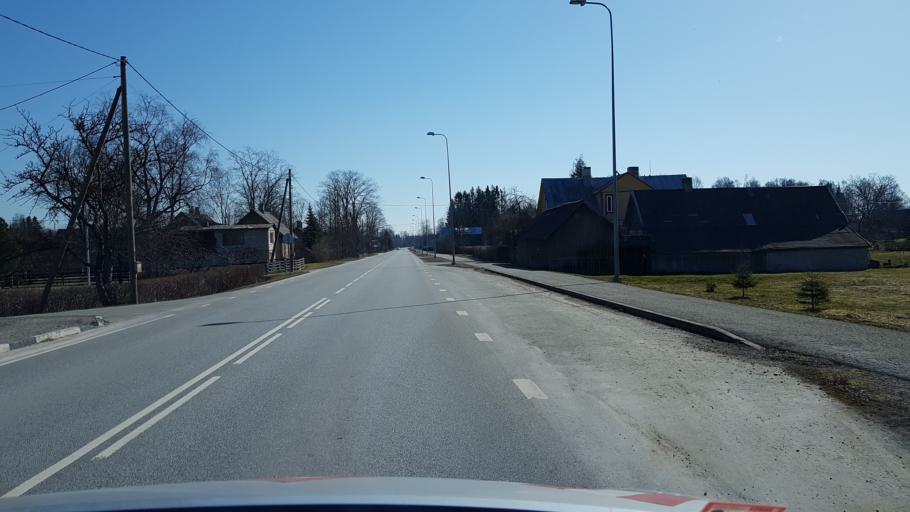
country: EE
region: Ida-Virumaa
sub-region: Aseri vald
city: Aseri
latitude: 59.3517
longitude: 26.8306
